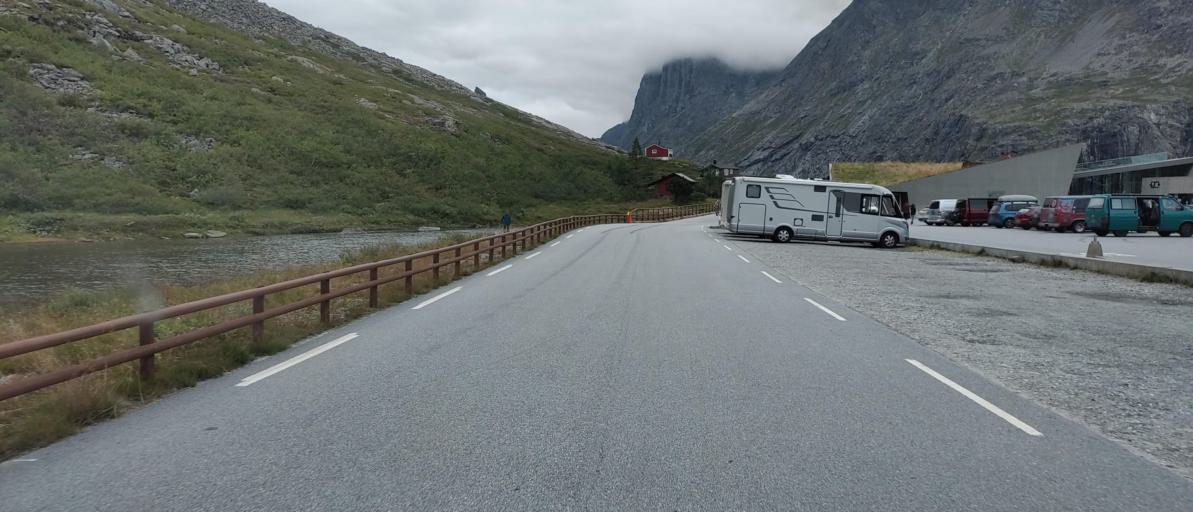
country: NO
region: More og Romsdal
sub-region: Rauma
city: Andalsnes
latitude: 62.4547
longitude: 7.6589
